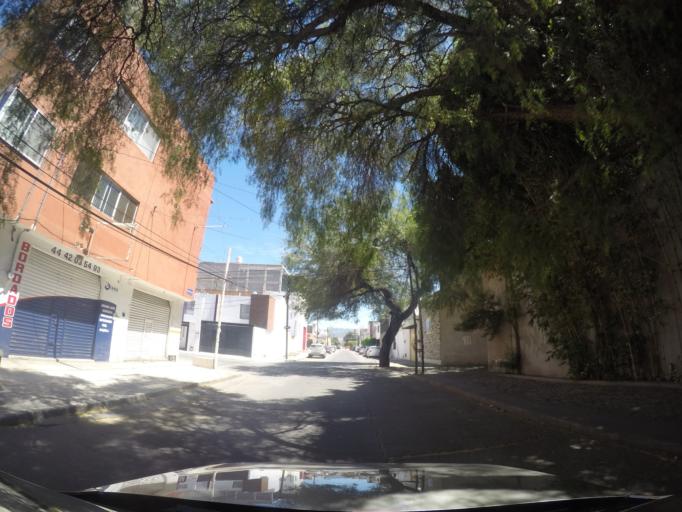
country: MX
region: San Luis Potosi
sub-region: San Luis Potosi
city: San Luis Potosi
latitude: 22.1570
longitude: -100.9940
